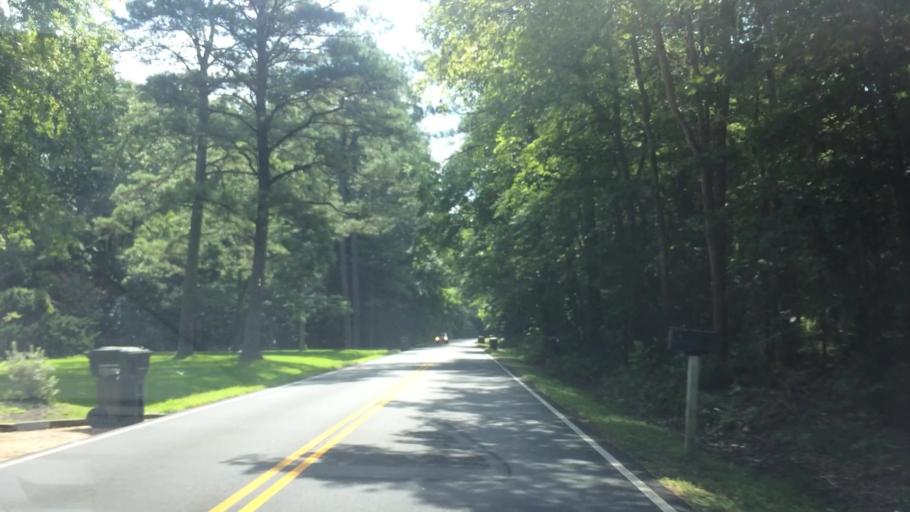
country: US
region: Virginia
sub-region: City of Poquoson
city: Poquoson
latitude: 37.1682
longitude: -76.4339
